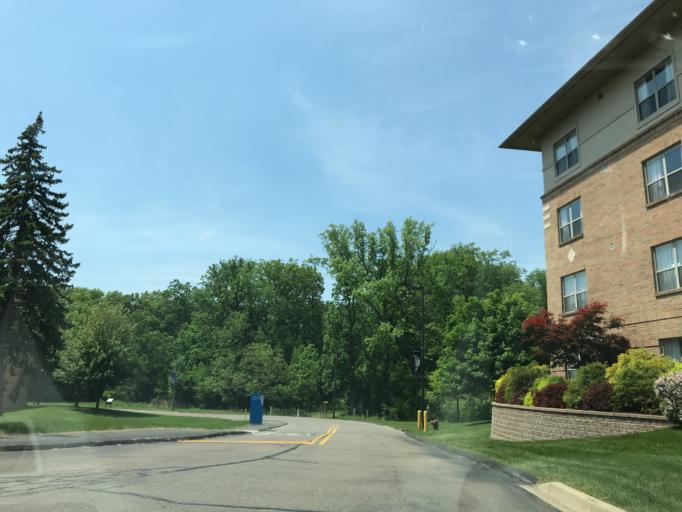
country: US
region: Michigan
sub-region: Oakland County
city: Southfield
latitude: 42.4757
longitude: -83.2507
